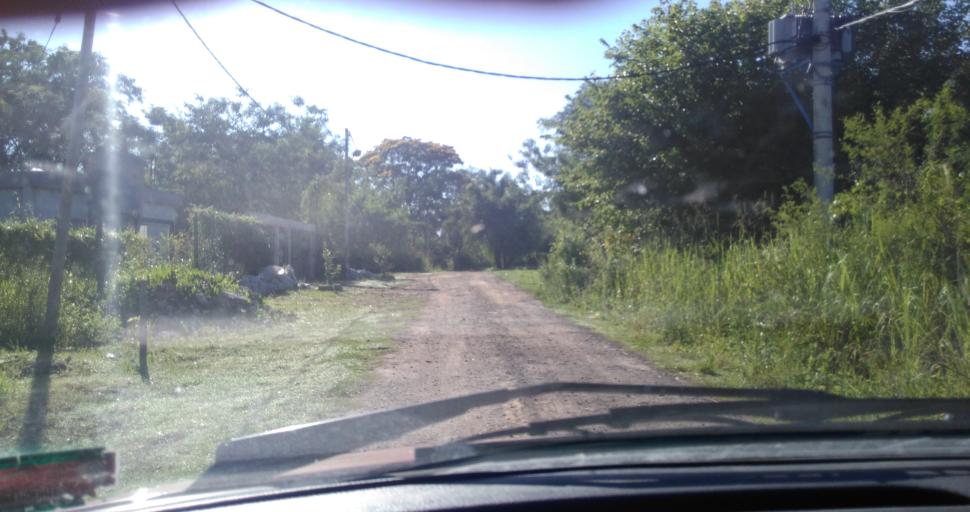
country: AR
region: Chaco
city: Resistencia
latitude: -27.4429
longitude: -58.9569
